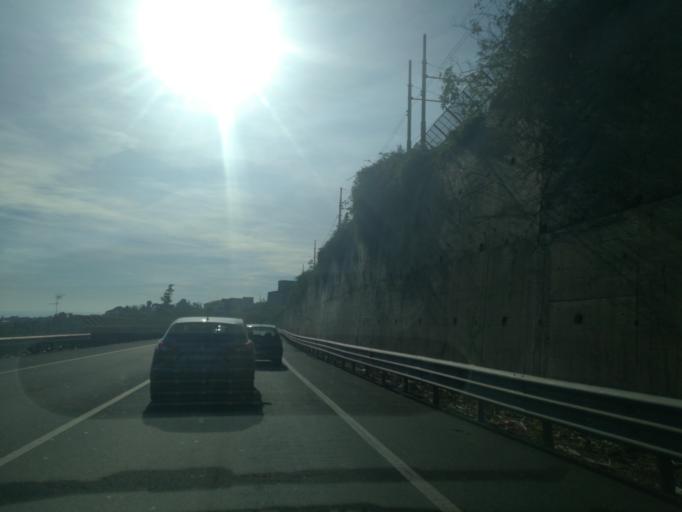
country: IT
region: Sicily
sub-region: Catania
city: Acireale
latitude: 37.6118
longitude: 15.1705
